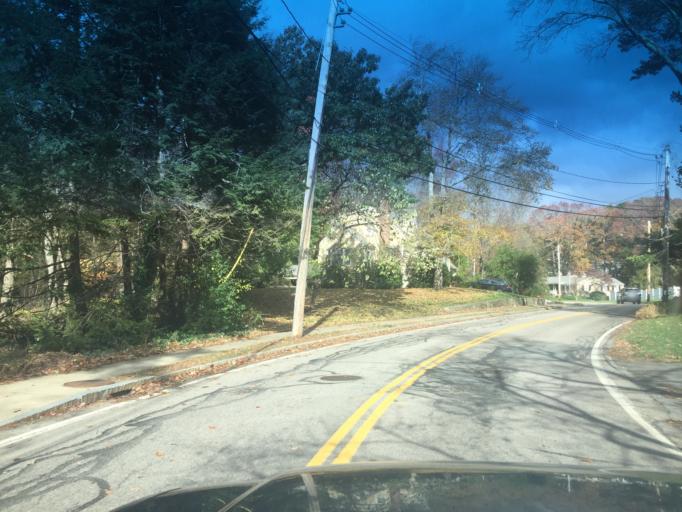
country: US
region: Massachusetts
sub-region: Norfolk County
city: Norwood
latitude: 42.2202
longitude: -71.1919
